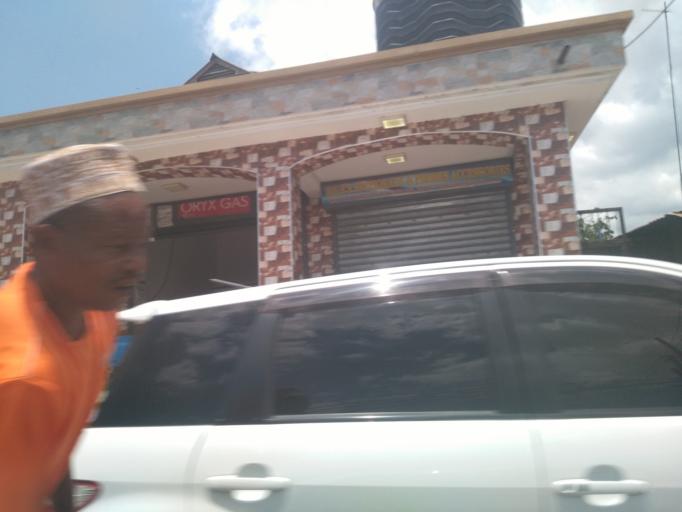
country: TZ
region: Dar es Salaam
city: Dar es Salaam
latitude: -6.8694
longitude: 39.2761
